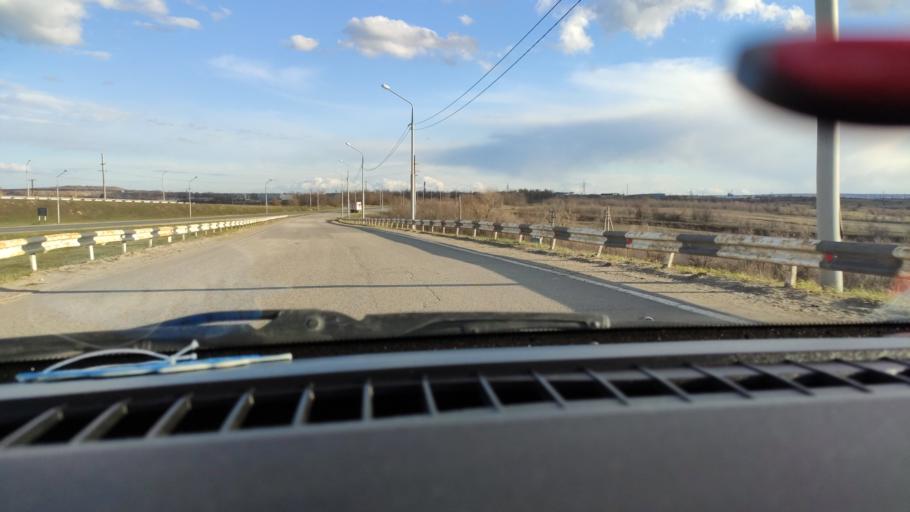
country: RU
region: Saratov
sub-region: Saratovskiy Rayon
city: Saratov
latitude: 51.6635
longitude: 45.9992
